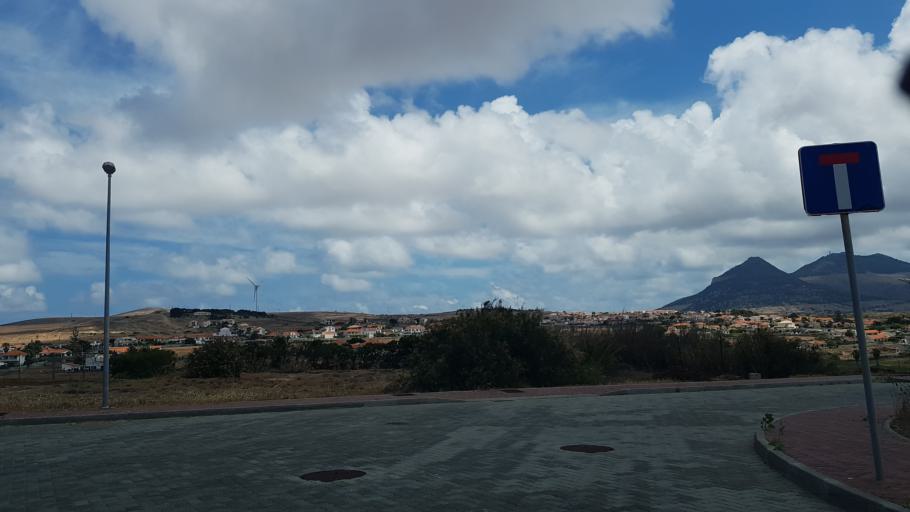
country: PT
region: Madeira
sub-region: Porto Santo
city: Vila de Porto Santo
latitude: 33.0498
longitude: -16.3617
